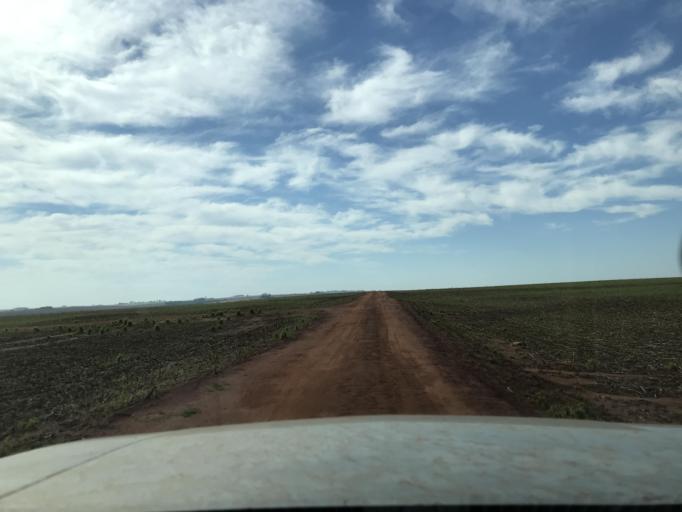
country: BR
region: Parana
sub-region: Palotina
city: Palotina
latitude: -24.1903
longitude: -53.8314
